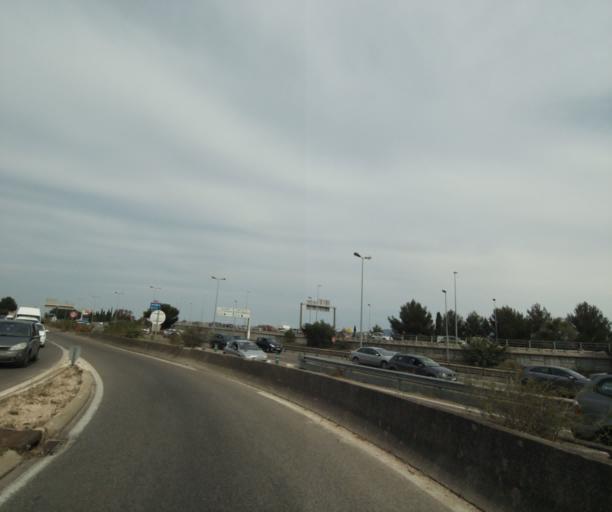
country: FR
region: Provence-Alpes-Cote d'Azur
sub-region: Departement du Var
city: La Garde
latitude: 43.1414
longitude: 6.0027
